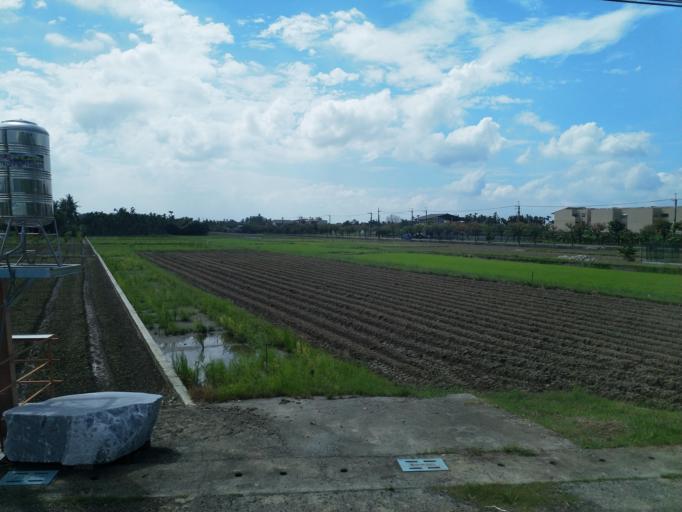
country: TW
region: Taiwan
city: Yujing
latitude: 22.9045
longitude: 120.5517
